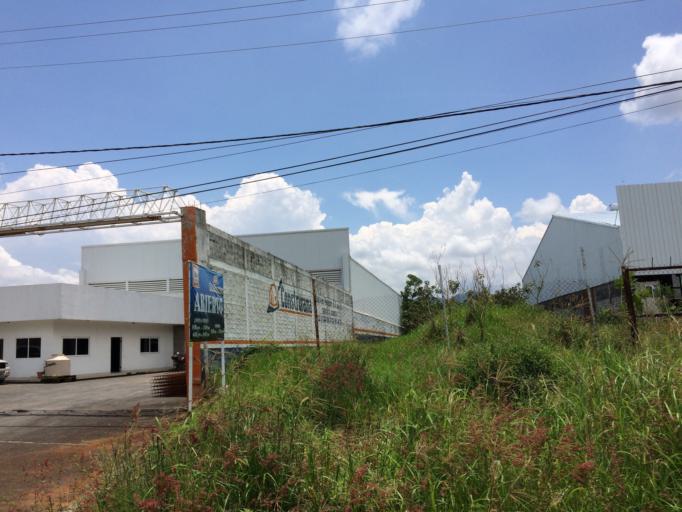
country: MX
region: Michoacan
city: Periban de Ramos
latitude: 19.5367
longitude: -102.4126
